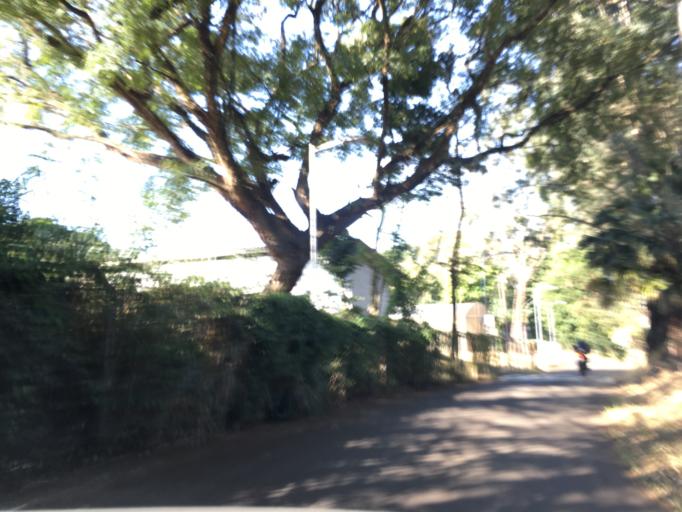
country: BR
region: Sao Paulo
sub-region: Piracicaba
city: Piracicaba
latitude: -22.7140
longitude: -47.6283
